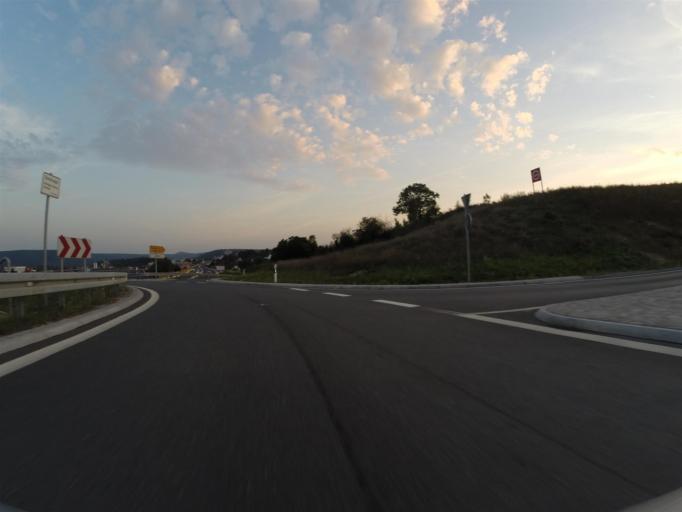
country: DE
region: Thuringia
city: Sulza
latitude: 50.8708
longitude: 11.5974
